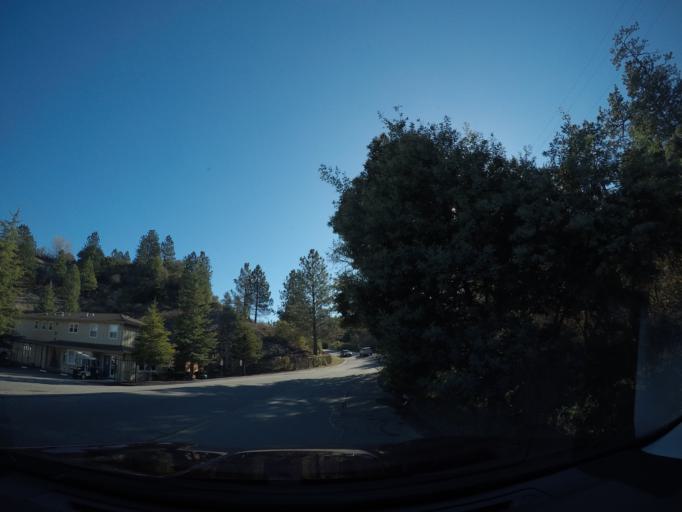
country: US
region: California
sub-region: Santa Cruz County
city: Mount Hermon
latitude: 37.0523
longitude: -122.0369
